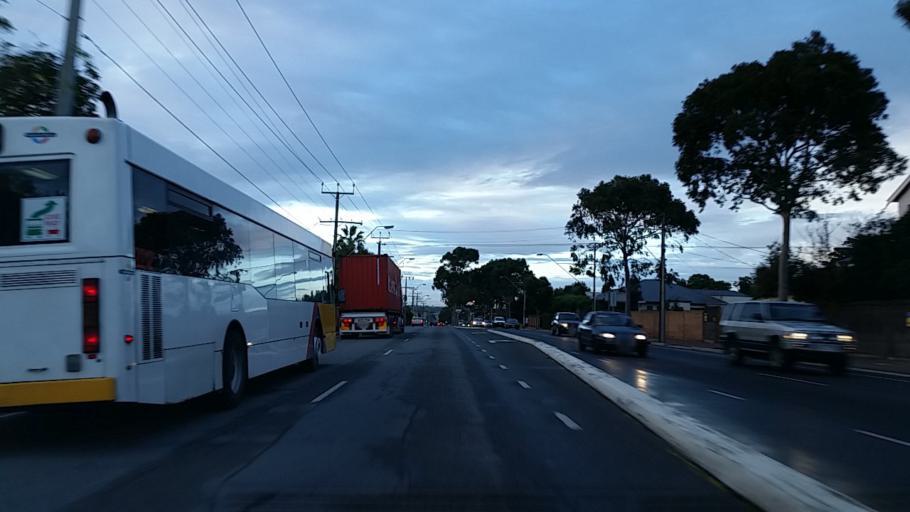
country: AU
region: South Australia
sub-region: Adelaide Hills
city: Seacliff
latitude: -35.0337
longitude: 138.5242
